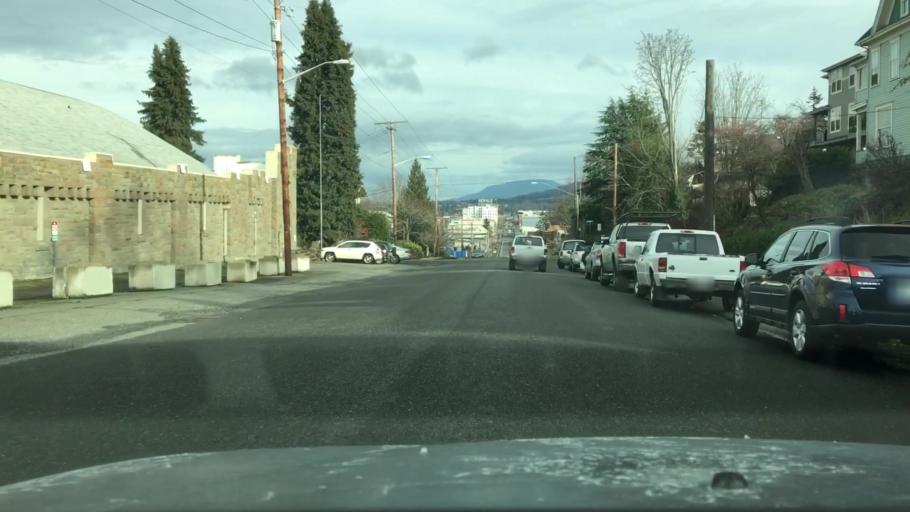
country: US
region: Washington
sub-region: Whatcom County
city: Bellingham
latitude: 48.7408
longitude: -122.4883
